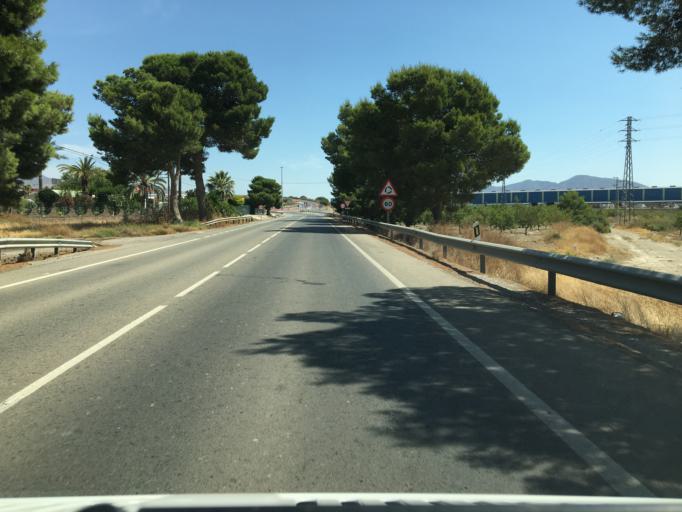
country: ES
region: Andalusia
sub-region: Provincia de Almeria
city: Huercal-Overa
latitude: 37.4321
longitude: -1.9114
